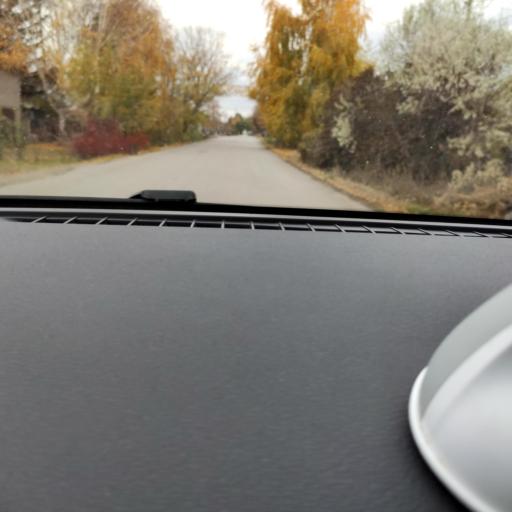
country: RU
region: Samara
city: Petra-Dubrava
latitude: 53.2428
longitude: 50.3187
